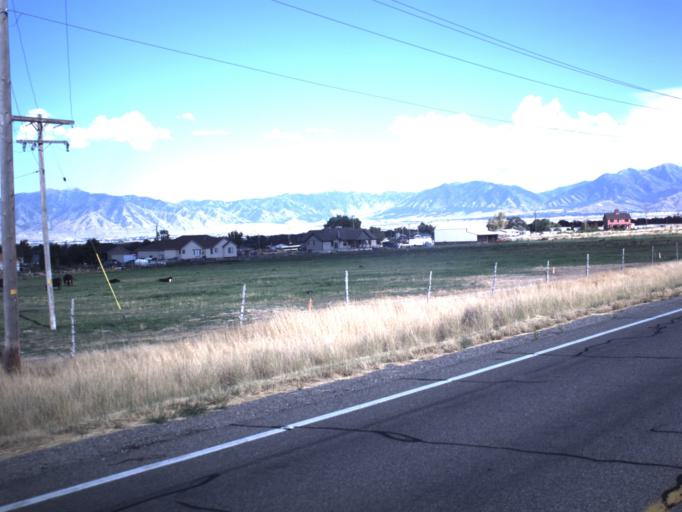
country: US
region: Utah
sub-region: Tooele County
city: Grantsville
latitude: 40.6100
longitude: -112.4924
